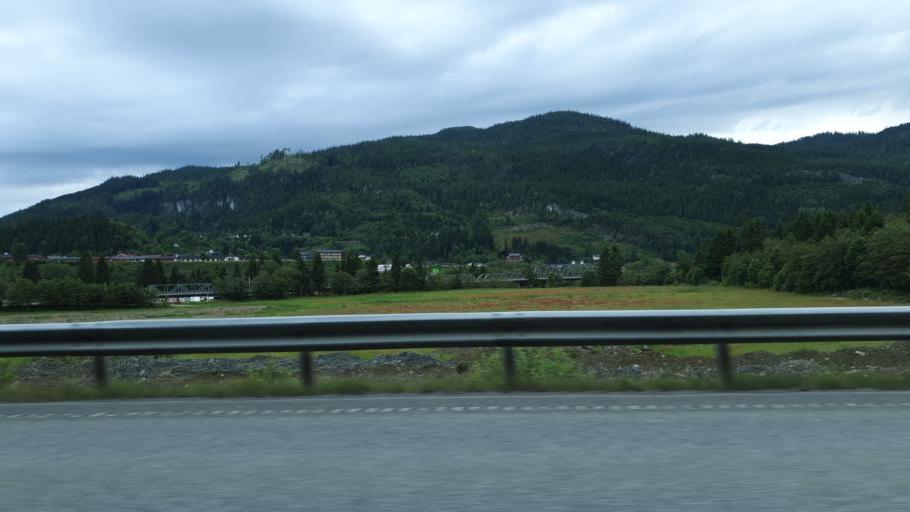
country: NO
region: Sor-Trondelag
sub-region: Midtre Gauldal
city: Storen
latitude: 63.0420
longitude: 10.2992
